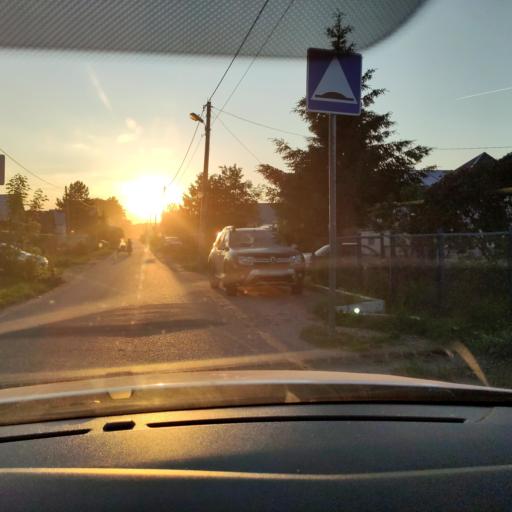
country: RU
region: Tatarstan
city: Stolbishchi
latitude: 55.7487
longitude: 49.3013
